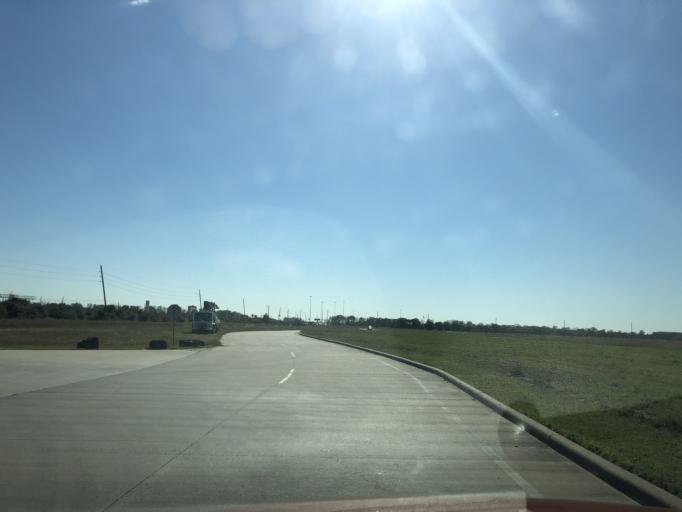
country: US
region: Texas
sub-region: Brazoria County
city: Brookside Village
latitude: 29.5932
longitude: -95.3881
